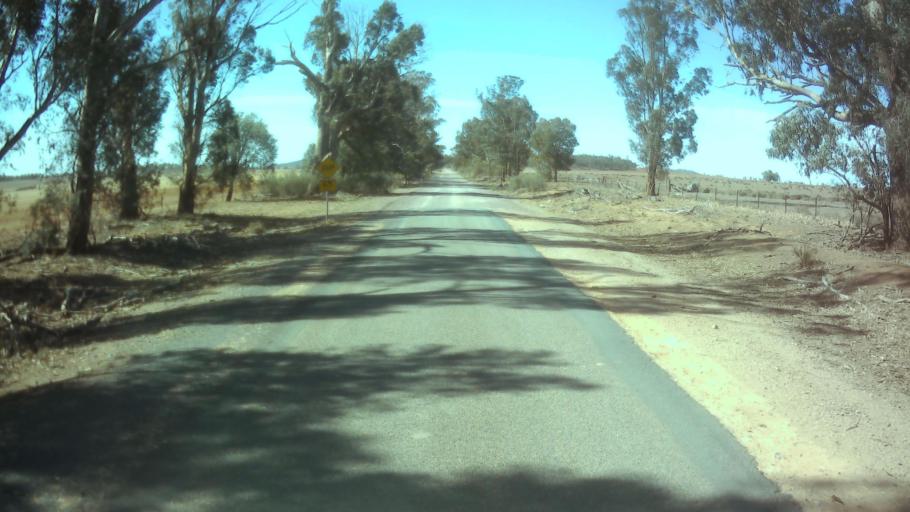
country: AU
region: New South Wales
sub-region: Forbes
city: Forbes
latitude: -33.7227
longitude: 147.7450
